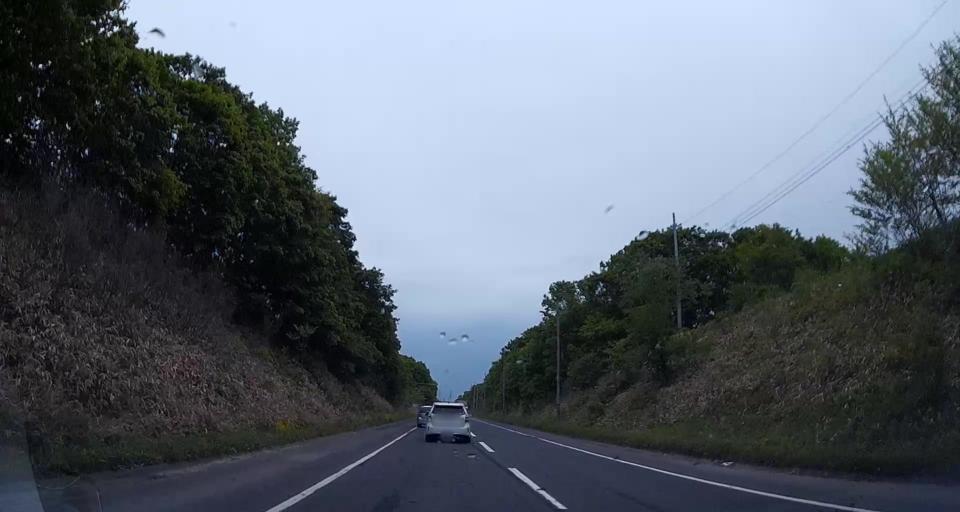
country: JP
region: Hokkaido
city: Chitose
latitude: 42.7051
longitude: 141.7437
